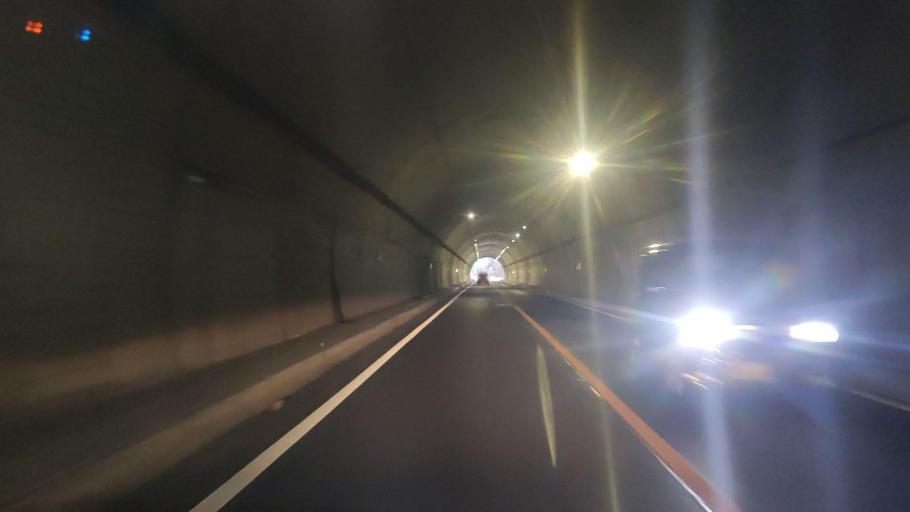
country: JP
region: Miyazaki
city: Nobeoka
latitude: 32.6302
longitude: 131.7216
